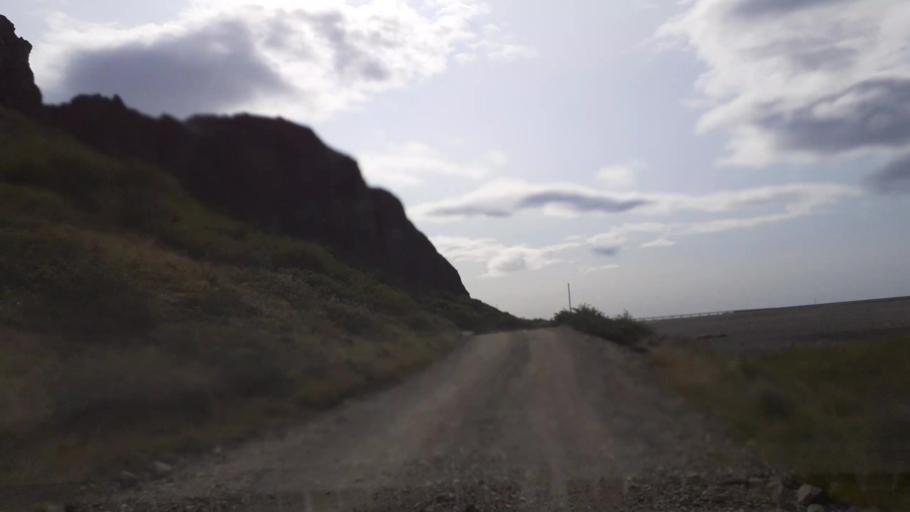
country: IS
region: East
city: Hoefn
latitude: 64.4331
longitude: -14.8928
